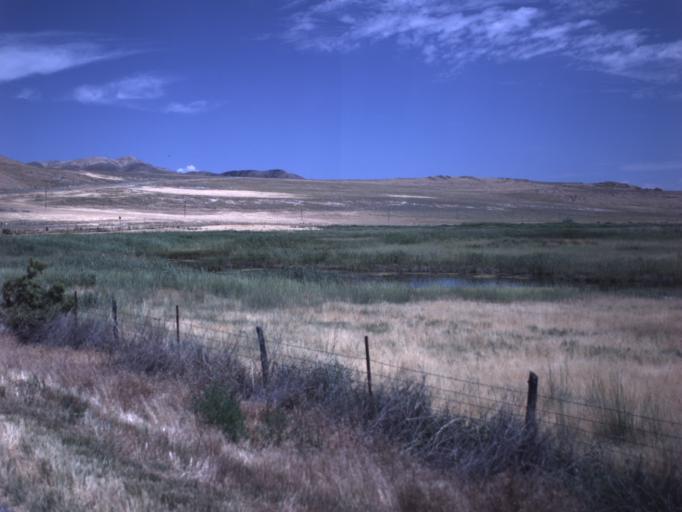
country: US
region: Utah
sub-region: Box Elder County
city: Tremonton
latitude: 41.6155
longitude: -112.3671
